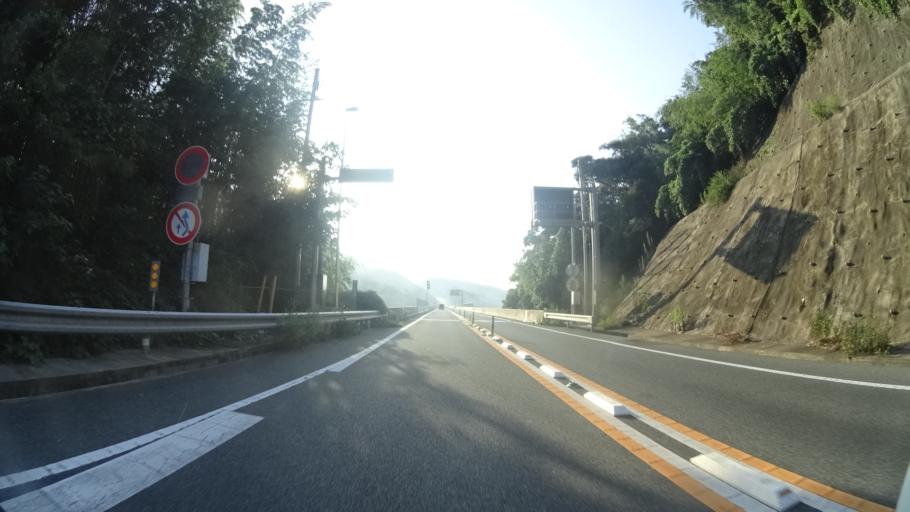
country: JP
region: Yamaguchi
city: Hagi
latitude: 34.3866
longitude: 131.3442
